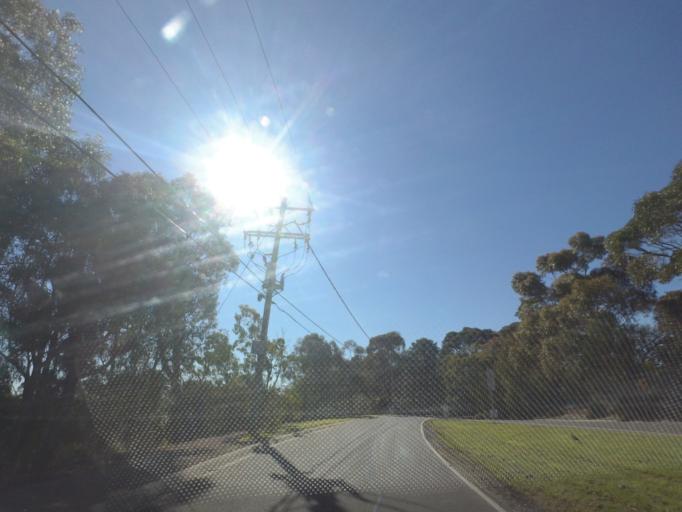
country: AU
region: Victoria
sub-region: Maroondah
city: Croydon Hills
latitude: -37.7656
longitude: 145.2714
